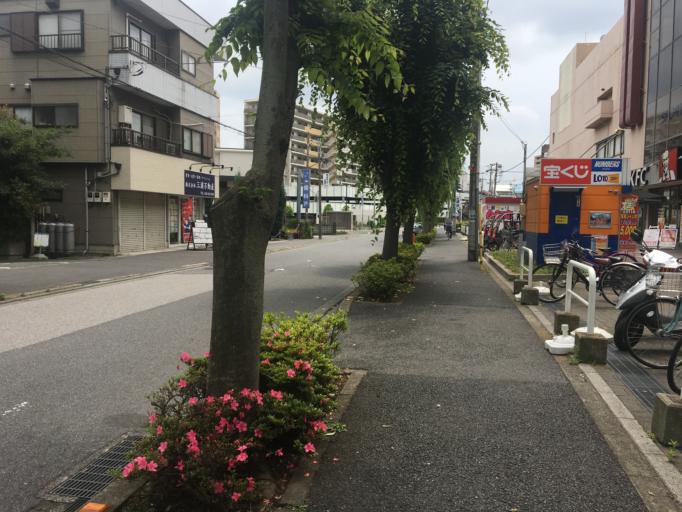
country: JP
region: Saitama
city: Kawaguchi
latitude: 35.8009
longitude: 139.7281
